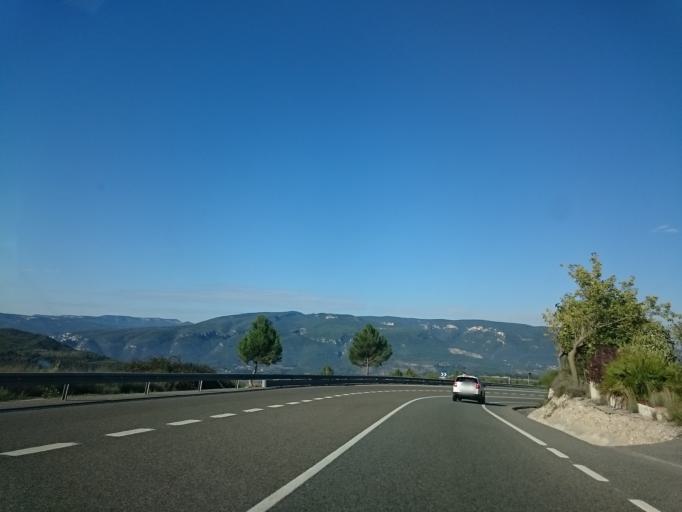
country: ES
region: Catalonia
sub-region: Provincia de Tarragona
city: Montblanc
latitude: 41.3476
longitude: 1.2154
